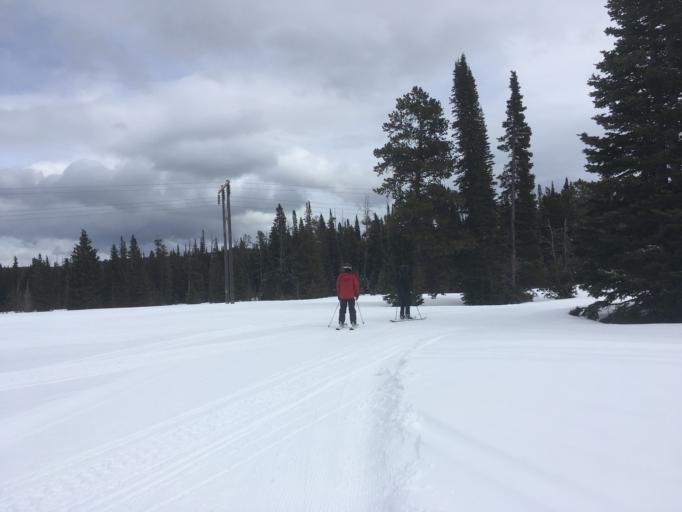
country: US
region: Montana
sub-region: Meagher County
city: White Sulphur Springs
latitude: 46.8519
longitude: -110.7014
